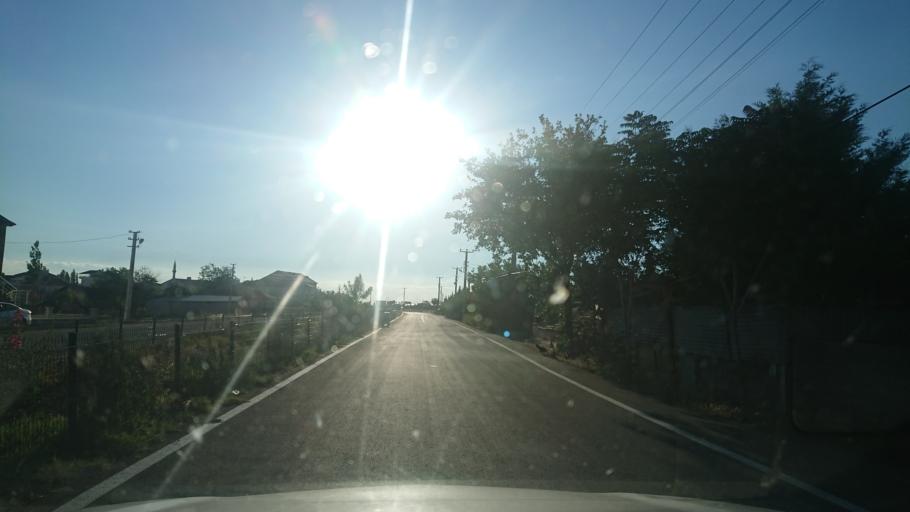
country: TR
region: Aksaray
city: Aksaray
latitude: 38.3907
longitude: 33.9942
